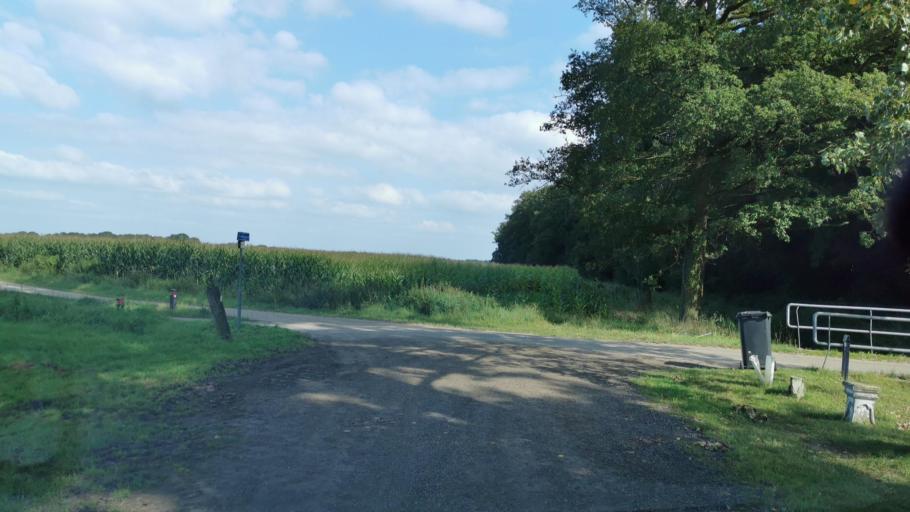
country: NL
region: Overijssel
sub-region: Gemeente Borne
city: Borne
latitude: 52.3186
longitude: 6.7888
